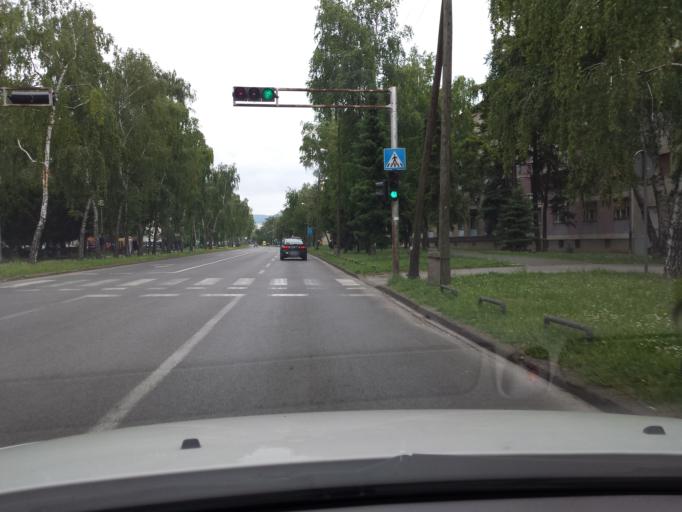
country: HR
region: Grad Zagreb
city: Zagreb - Centar
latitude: 45.8016
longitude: 15.9516
